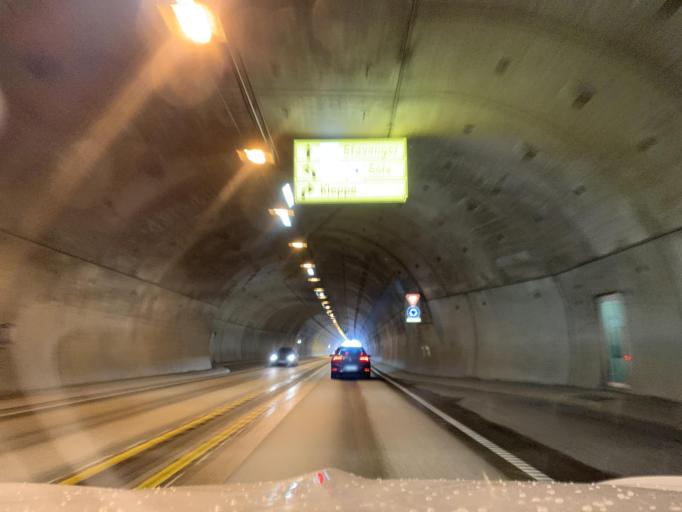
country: NO
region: Rogaland
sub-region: Klepp
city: Kleppe
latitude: 58.7750
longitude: 5.6194
